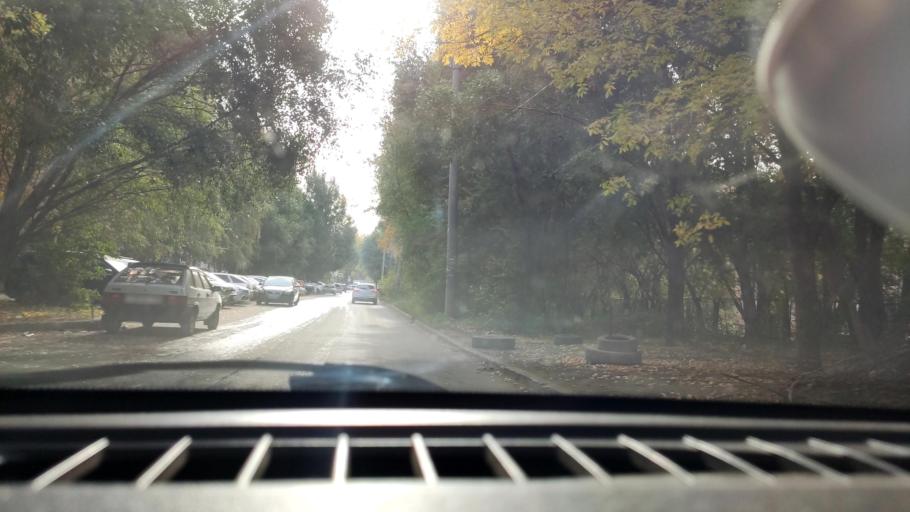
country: RU
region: Samara
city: Samara
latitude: 53.2324
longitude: 50.2498
